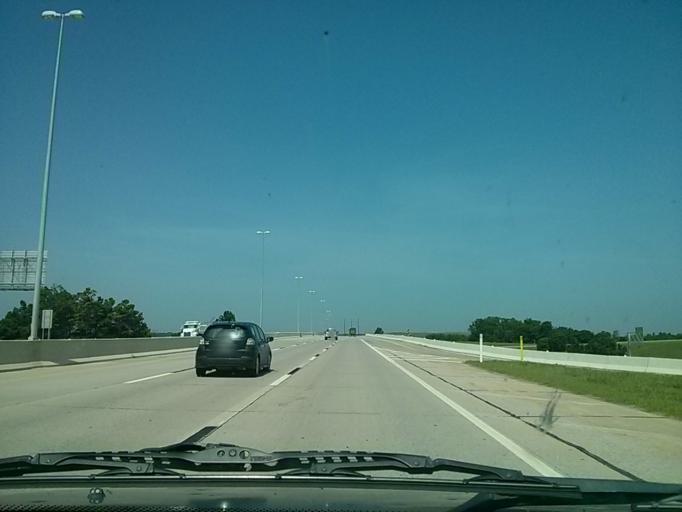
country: US
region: Oklahoma
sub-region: Tulsa County
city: Jenks
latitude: 36.0099
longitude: -96.0099
